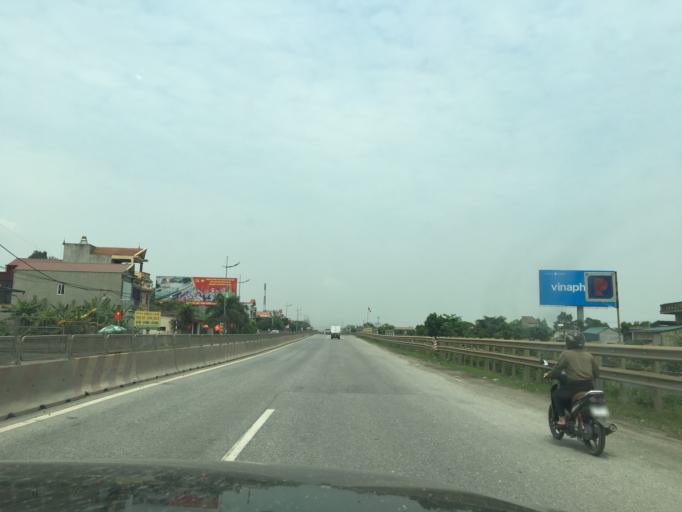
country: VN
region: Ninh Binh
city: Thi Tran Tam Diep
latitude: 20.1770
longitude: 105.9503
